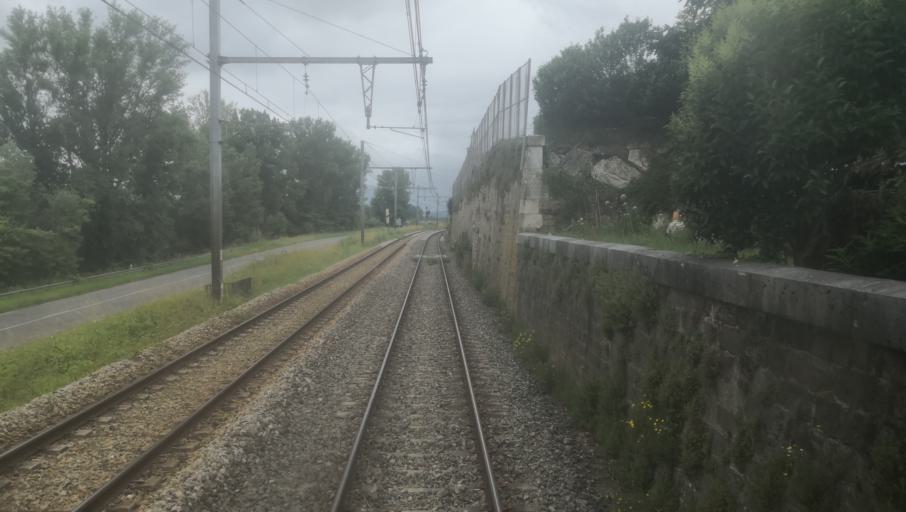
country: FR
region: Aquitaine
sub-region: Departement du Lot-et-Garonne
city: Port-Sainte-Marie
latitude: 44.2503
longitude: 0.4007
